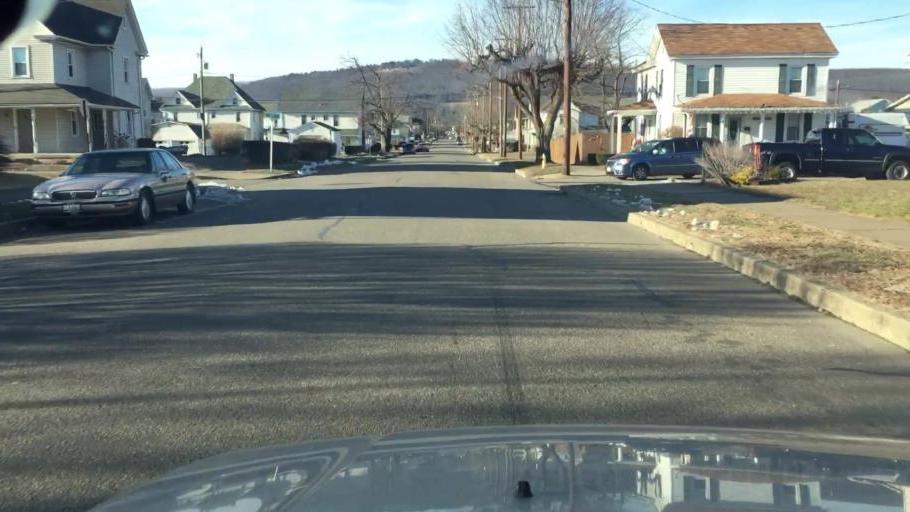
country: US
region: Pennsylvania
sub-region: Columbia County
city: Berwick
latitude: 41.0607
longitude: -76.2313
